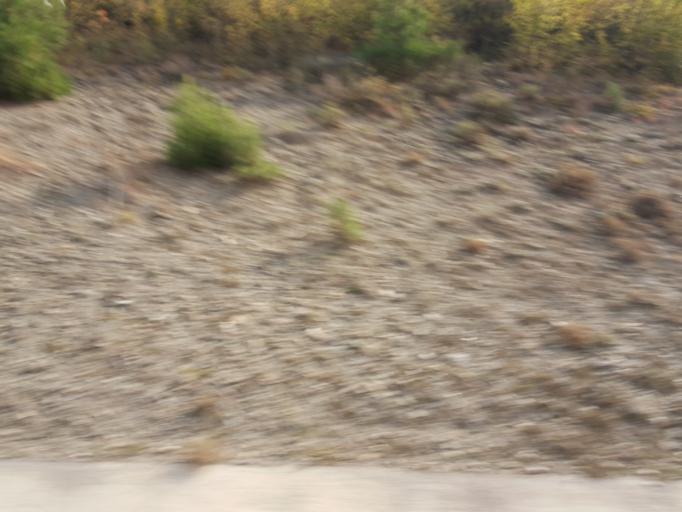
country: TR
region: Sinop
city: Sarayduzu
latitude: 41.3485
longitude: 34.8815
